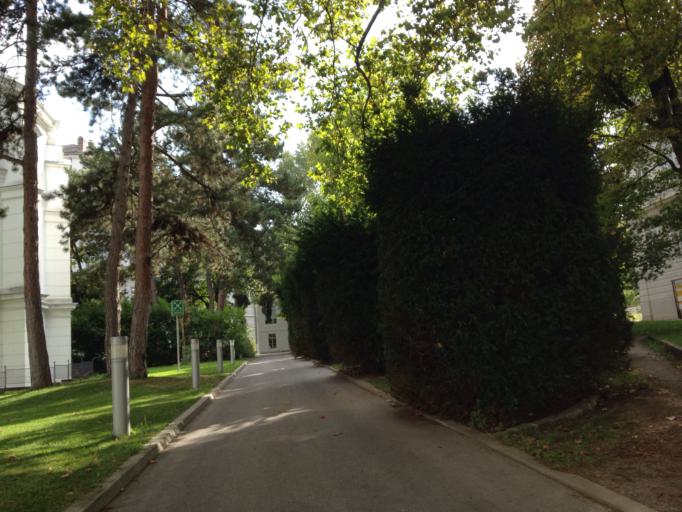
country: AT
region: Vienna
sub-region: Wien Stadt
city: Vienna
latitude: 48.2201
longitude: 16.3511
